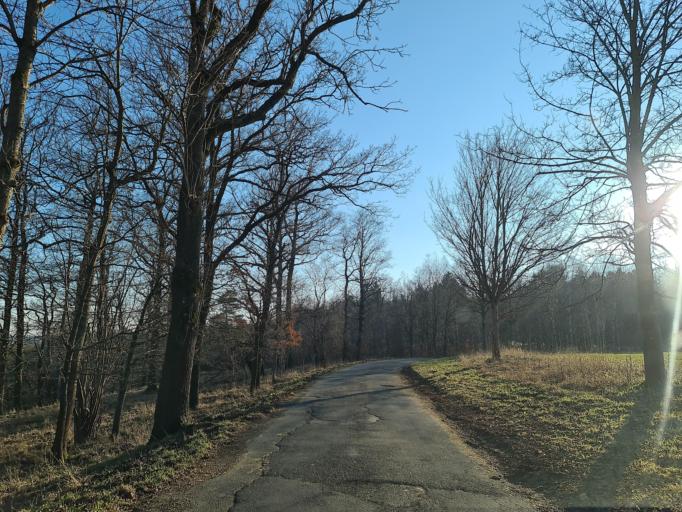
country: DE
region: Saxony
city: Pohl
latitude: 50.5332
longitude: 12.1686
